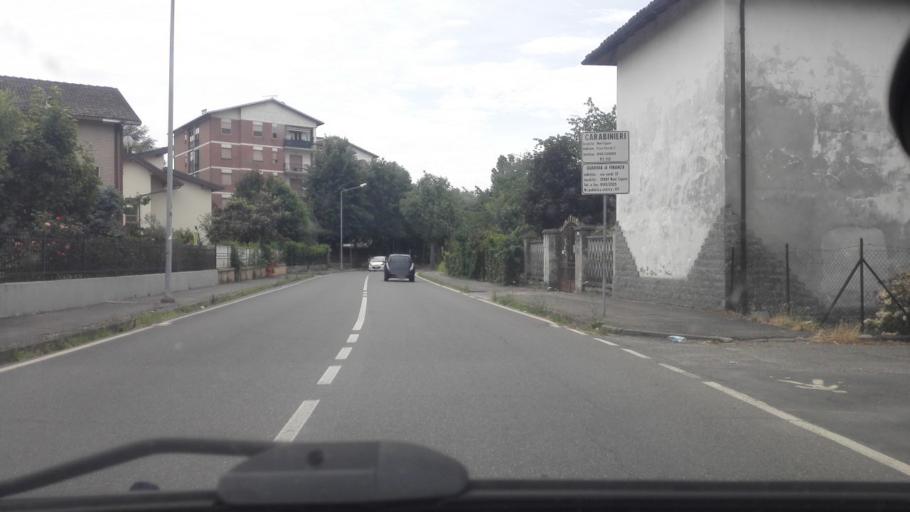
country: IT
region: Piedmont
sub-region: Provincia di Alessandria
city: Novi Ligure
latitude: 44.7715
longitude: 8.8004
